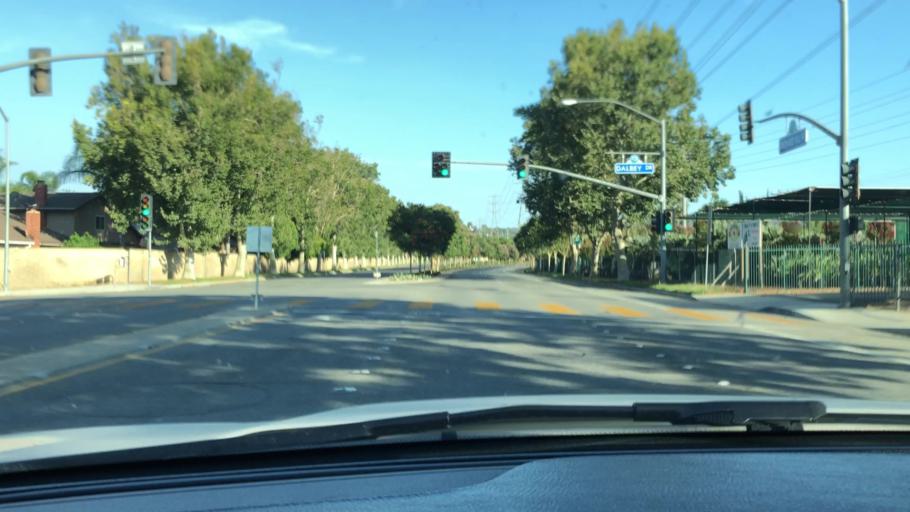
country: US
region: California
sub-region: Los Angeles County
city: Santa Clarita
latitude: 34.3852
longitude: -118.5439
